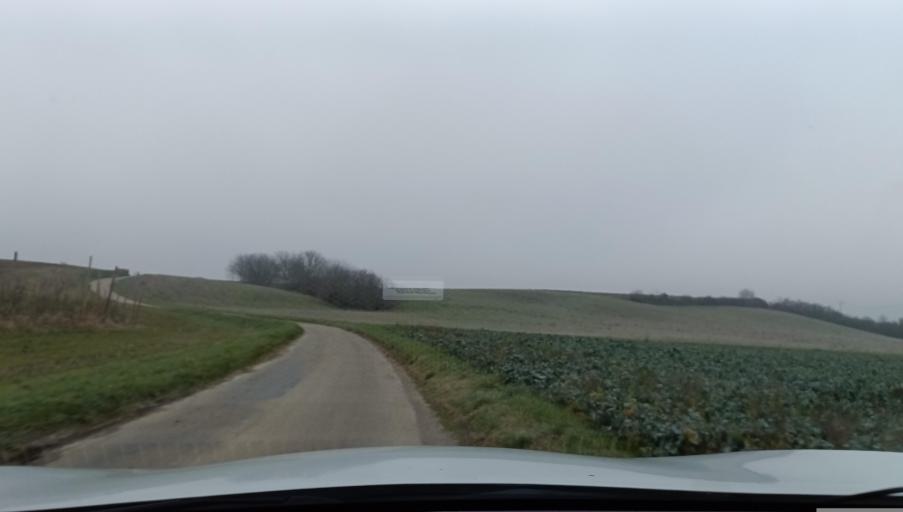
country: FR
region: Rhone-Alpes
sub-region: Departement de l'Isere
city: Seyssuel
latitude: 45.5732
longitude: 4.8552
